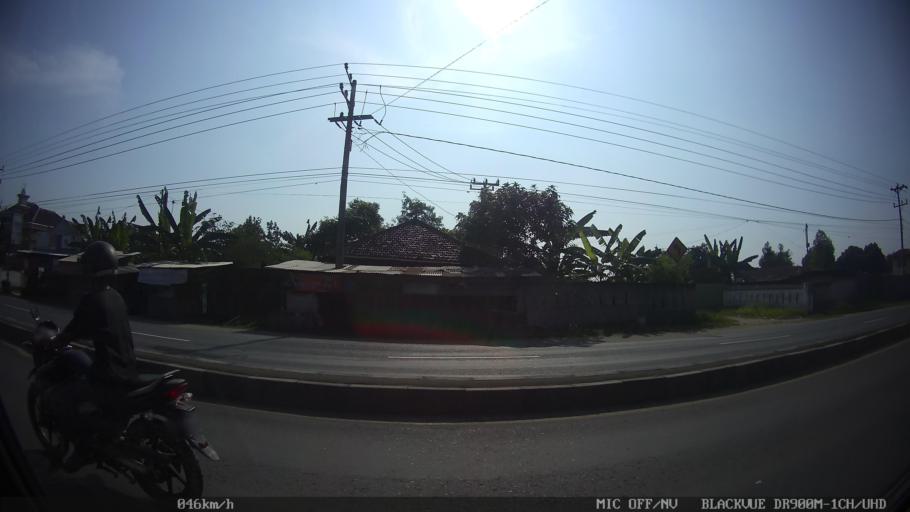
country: ID
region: Lampung
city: Natar
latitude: -5.2748
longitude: 105.1873
